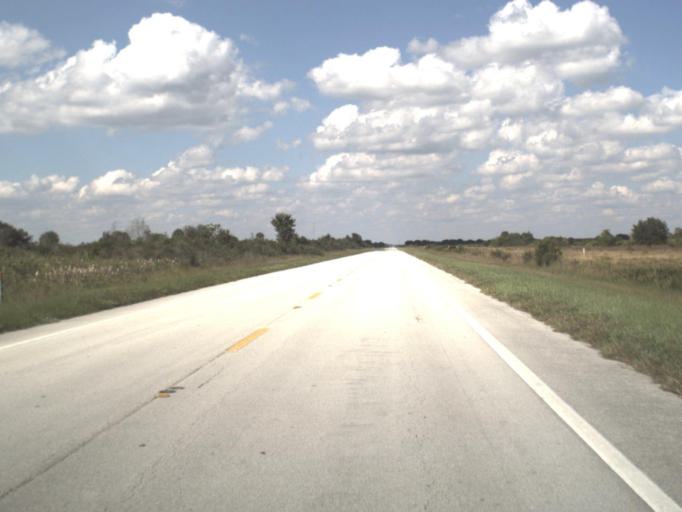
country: US
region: Florida
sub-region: Highlands County
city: Lake Placid
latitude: 27.4077
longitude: -81.1794
